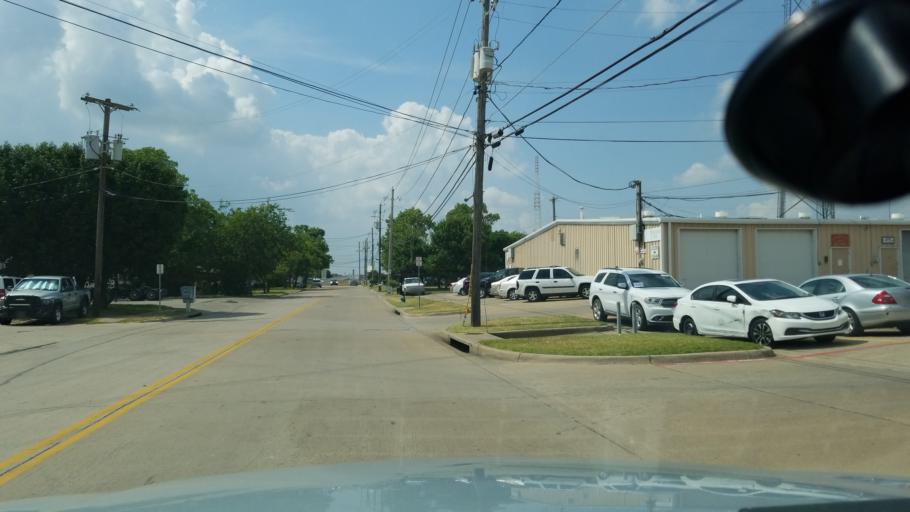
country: US
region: Texas
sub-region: Dallas County
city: Irving
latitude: 32.8328
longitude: -96.9116
